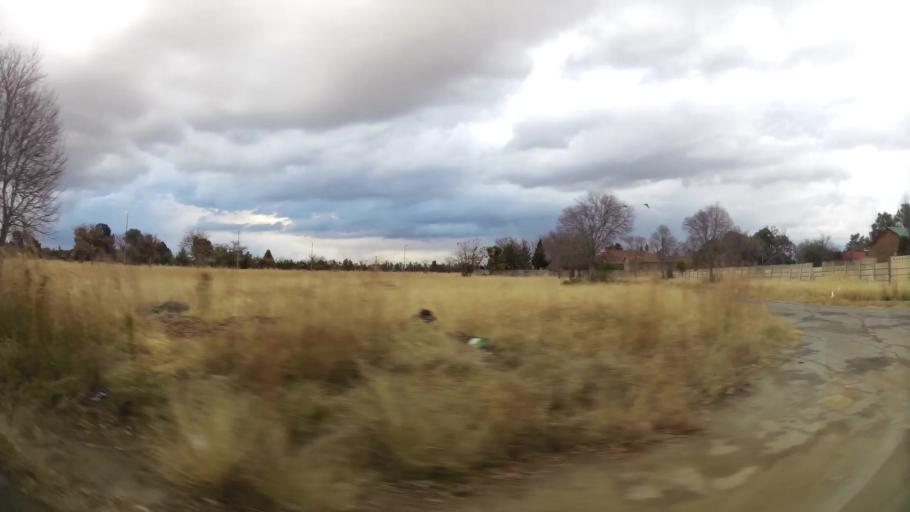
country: ZA
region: Orange Free State
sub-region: Lejweleputswa District Municipality
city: Welkom
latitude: -27.9632
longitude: 26.7195
